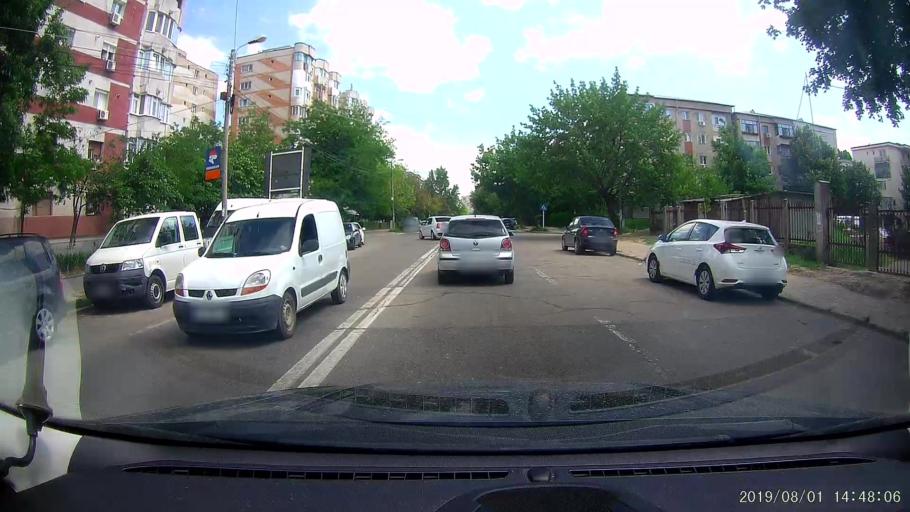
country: RO
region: Galati
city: Galati
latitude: 45.4126
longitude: 28.0070
